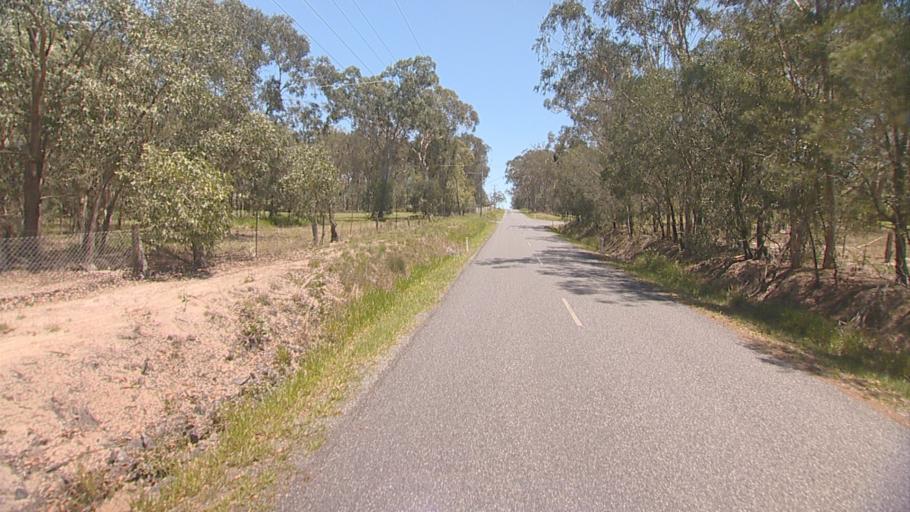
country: AU
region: Queensland
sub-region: Logan
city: Logan Reserve
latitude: -27.7333
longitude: 153.0827
